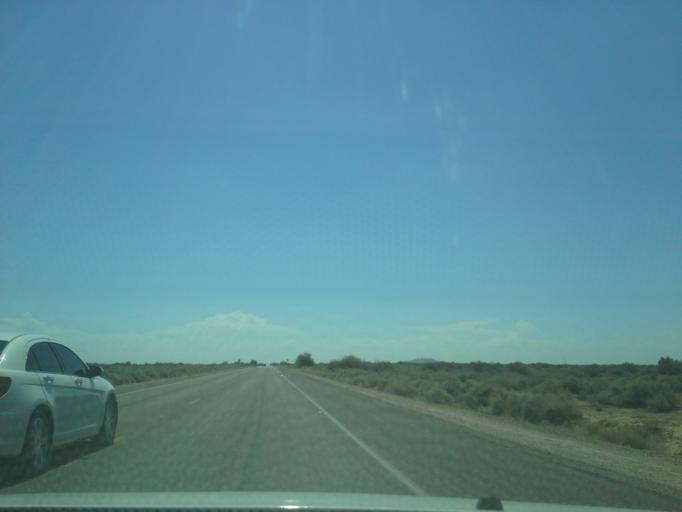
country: US
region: Arizona
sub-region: Maricopa County
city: Laveen
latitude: 33.2650
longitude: -112.1482
